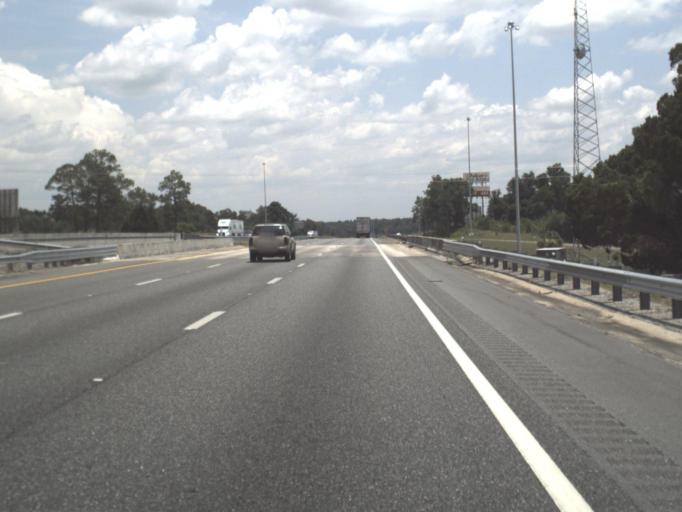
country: US
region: Florida
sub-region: Hamilton County
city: Jasper
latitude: 30.5184
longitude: -83.0592
